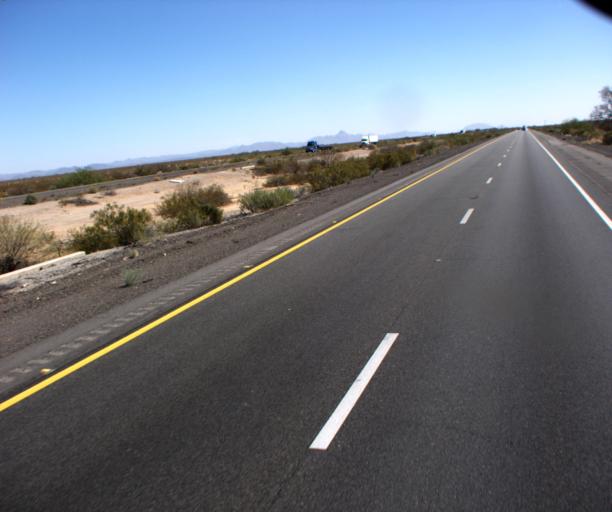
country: US
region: Arizona
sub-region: La Paz County
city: Salome
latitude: 33.5835
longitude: -113.4509
